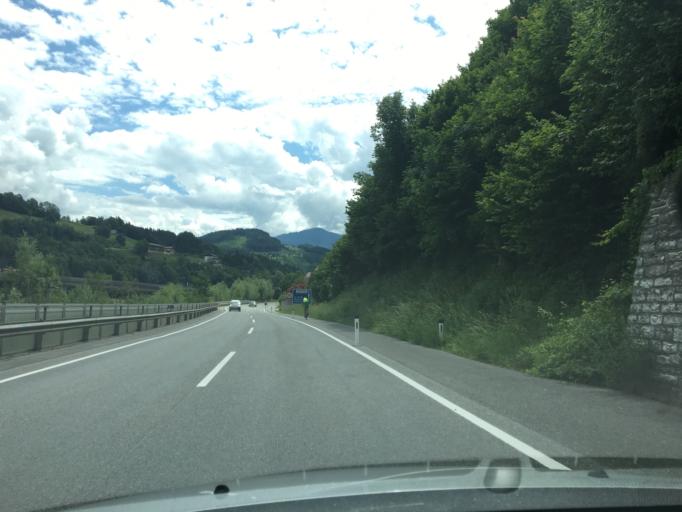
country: AT
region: Salzburg
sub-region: Politischer Bezirk Sankt Johann im Pongau
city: Werfen
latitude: 47.4687
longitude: 13.1950
